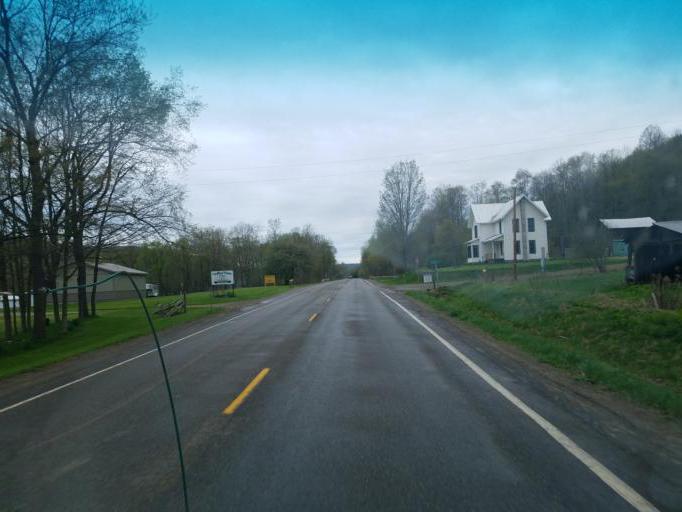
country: US
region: New York
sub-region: Allegany County
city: Andover
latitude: 42.0138
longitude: -77.8355
